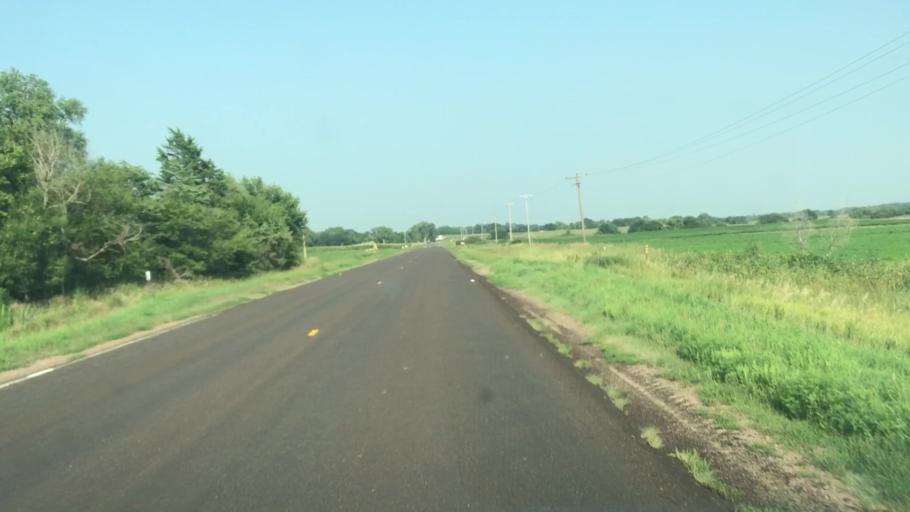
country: US
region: Nebraska
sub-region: Buffalo County
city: Ravenna
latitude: 41.0756
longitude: -98.7378
